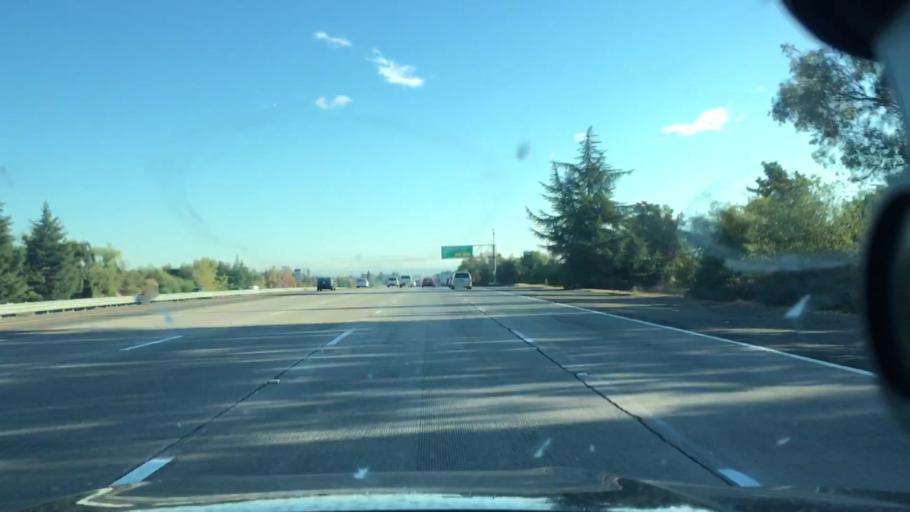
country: US
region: California
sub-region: Sacramento County
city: Antelope
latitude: 38.6942
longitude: -121.3237
